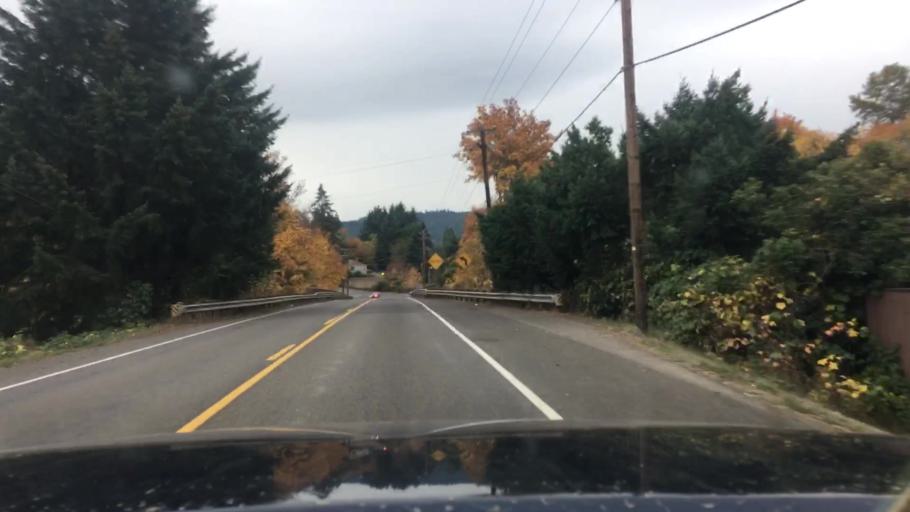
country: US
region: Oregon
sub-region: Lane County
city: Cottage Grove
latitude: 43.7642
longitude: -123.0657
